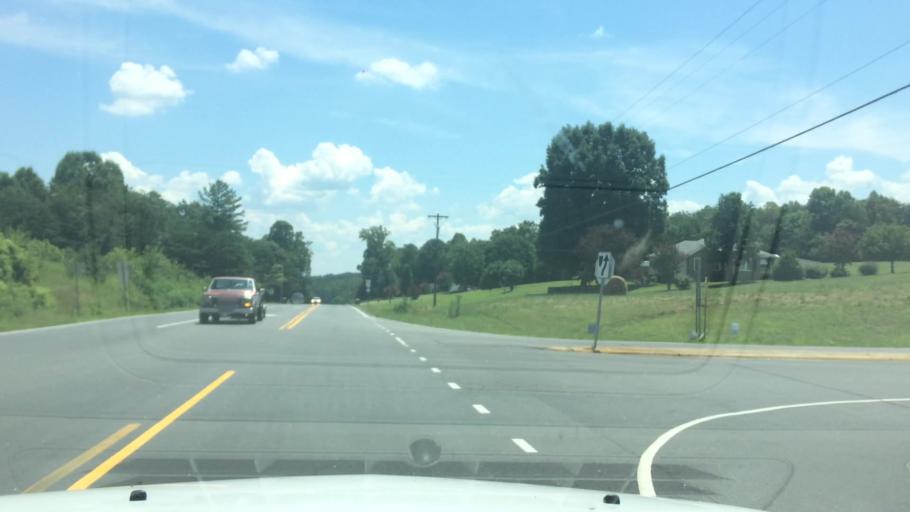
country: US
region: North Carolina
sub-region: Alexander County
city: Taylorsville
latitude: 35.9229
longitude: -81.2614
